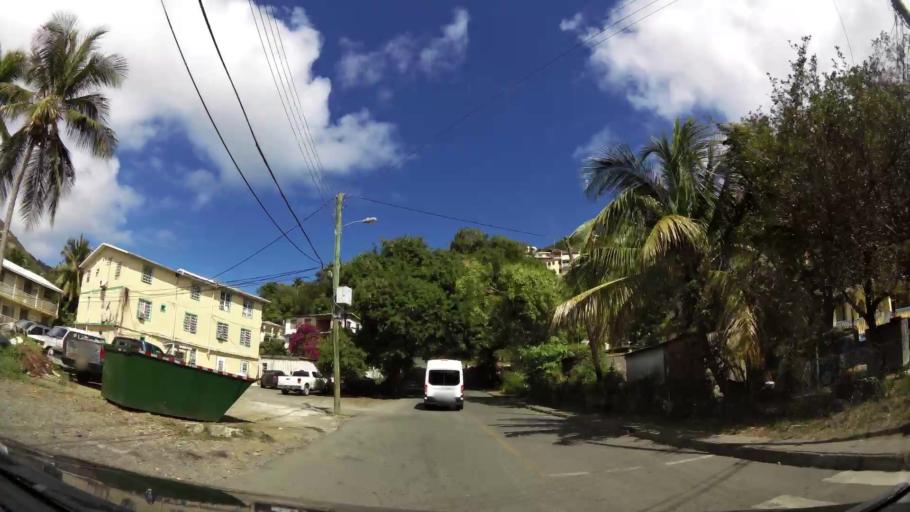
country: VG
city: Road Town
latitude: 18.4281
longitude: -64.6218
